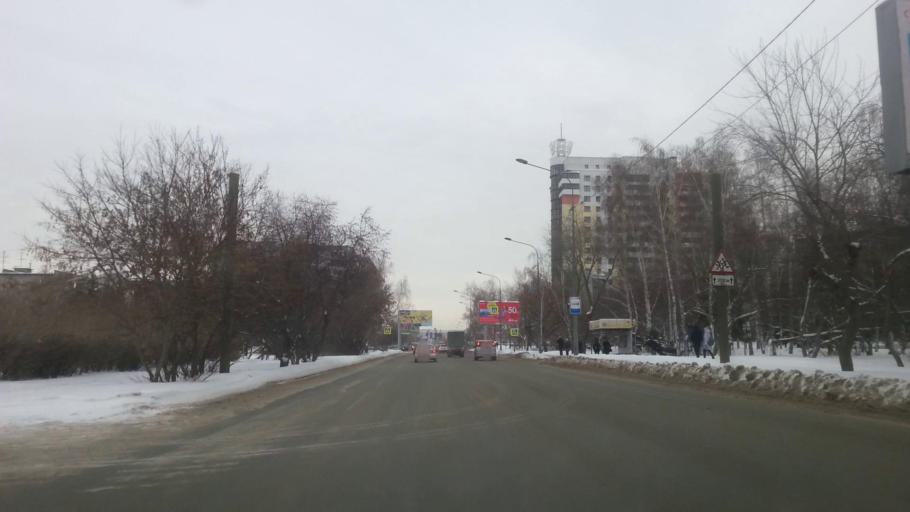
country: RU
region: Altai Krai
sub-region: Gorod Barnaulskiy
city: Barnaul
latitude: 53.3445
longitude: 83.7567
